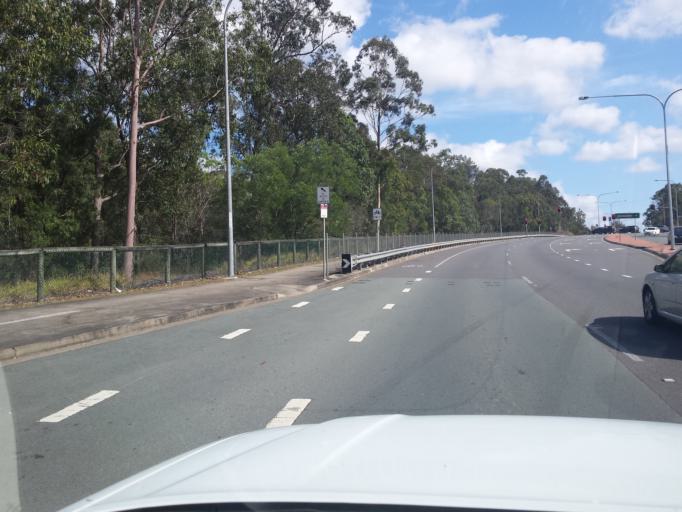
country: AU
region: Queensland
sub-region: Brisbane
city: Bridegman Downs
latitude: -27.3799
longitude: 152.9810
